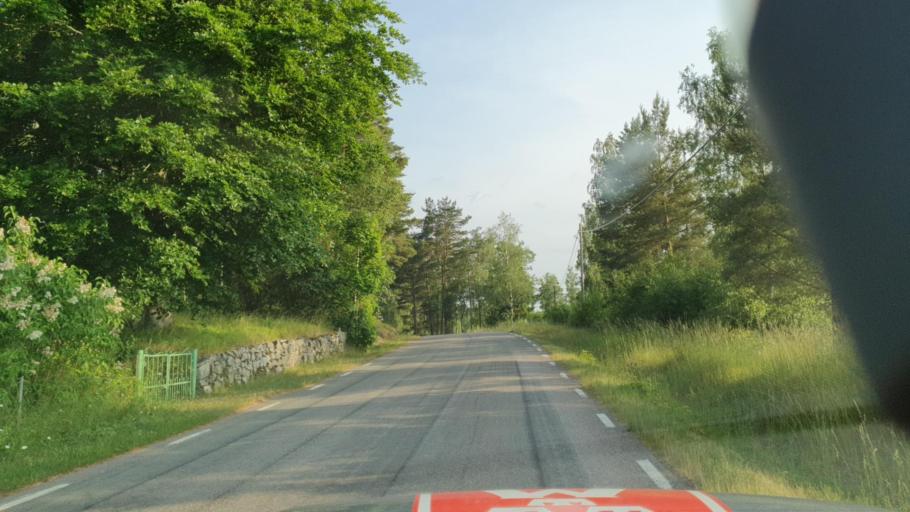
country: SE
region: Kalmar
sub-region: Torsas Kommun
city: Torsas
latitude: 56.4768
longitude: 16.0908
